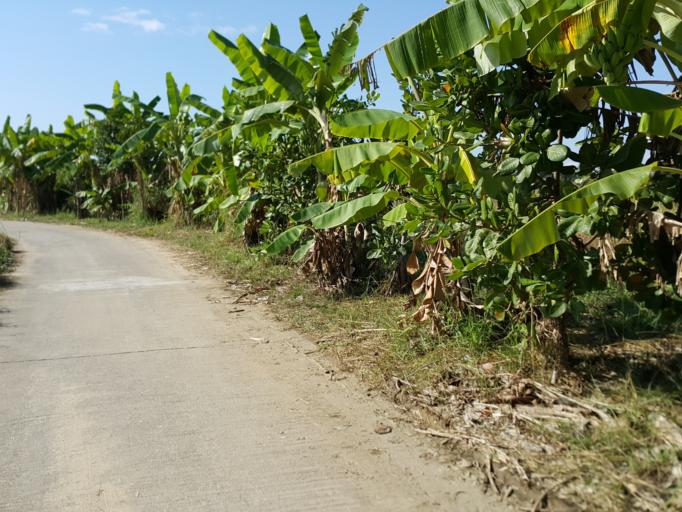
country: TH
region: Chiang Mai
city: San Kamphaeng
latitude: 18.7755
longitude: 99.0963
